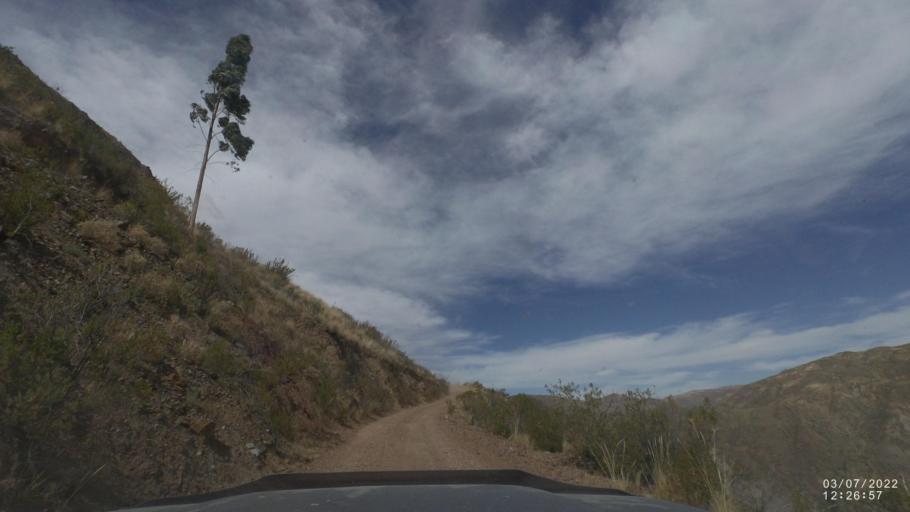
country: BO
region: Cochabamba
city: Irpa Irpa
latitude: -17.8094
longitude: -66.6152
